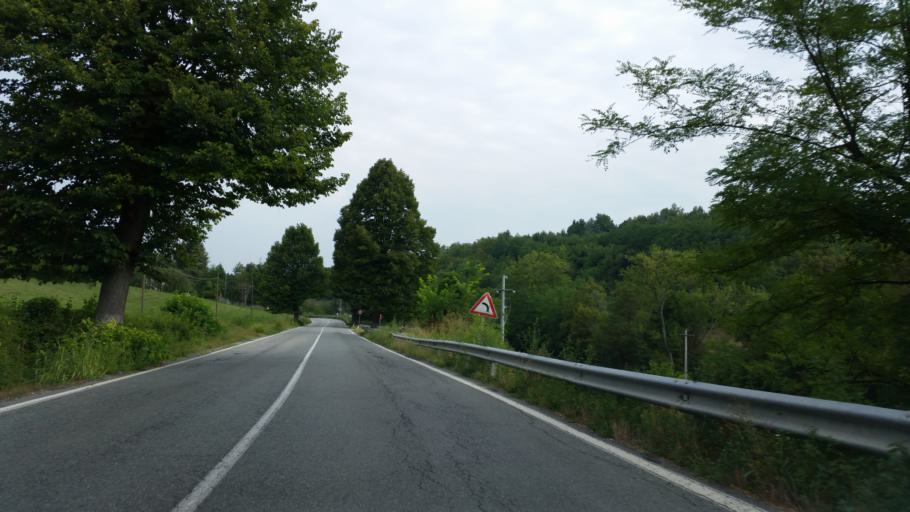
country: IT
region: Piedmont
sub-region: Provincia di Torino
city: Brozolo
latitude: 45.1280
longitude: 8.0592
